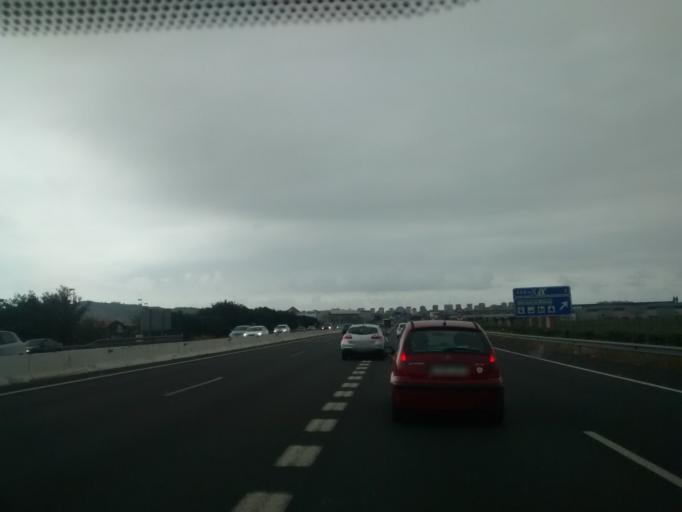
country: ES
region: Cantabria
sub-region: Provincia de Cantabria
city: El Astillero
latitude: 43.4295
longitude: -3.8362
